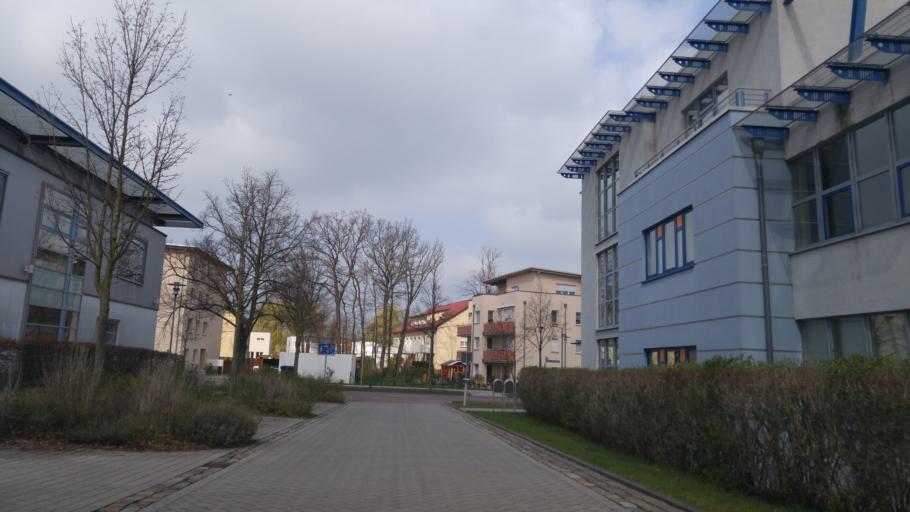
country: DE
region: Saxony-Anhalt
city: Halle Neustadt
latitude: 51.4936
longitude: 11.9344
